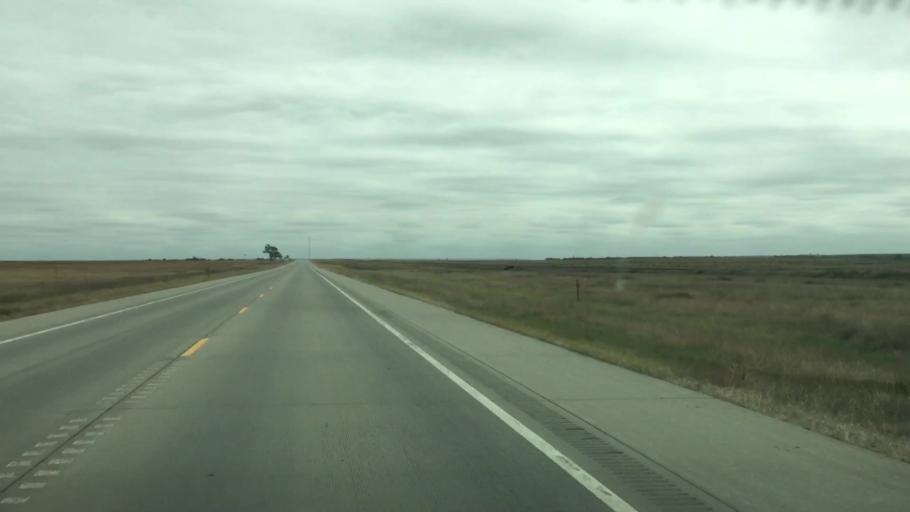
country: US
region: Colorado
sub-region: Kiowa County
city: Eads
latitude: 38.7651
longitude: -102.8381
